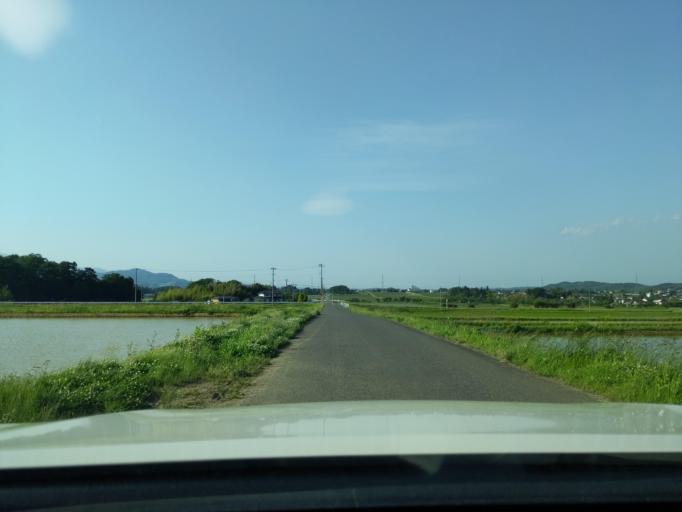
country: JP
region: Fukushima
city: Koriyama
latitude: 37.4411
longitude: 140.3629
